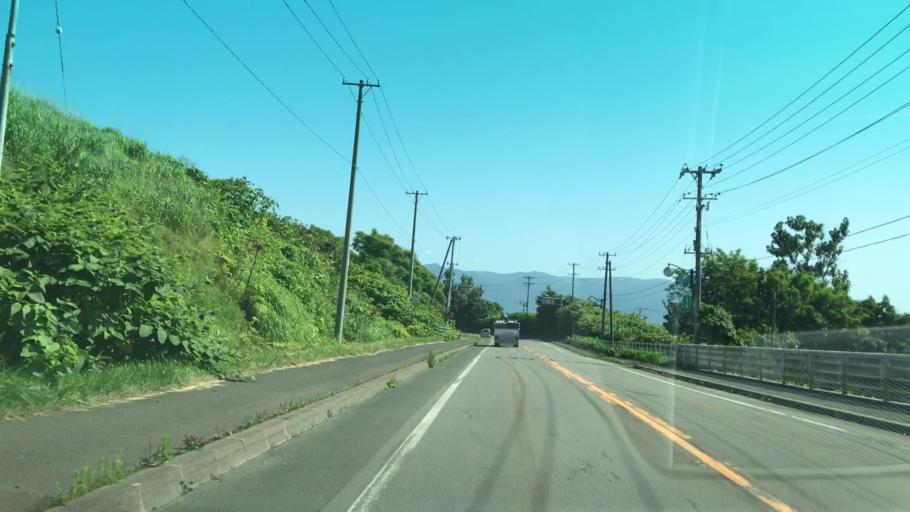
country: JP
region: Hokkaido
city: Iwanai
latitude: 43.0613
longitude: 140.4973
